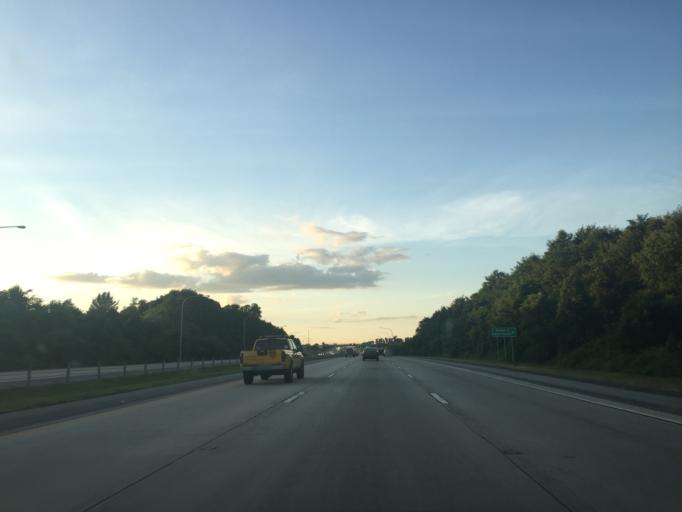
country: US
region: Delaware
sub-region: New Castle County
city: Bear
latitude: 39.5723
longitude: -75.6620
